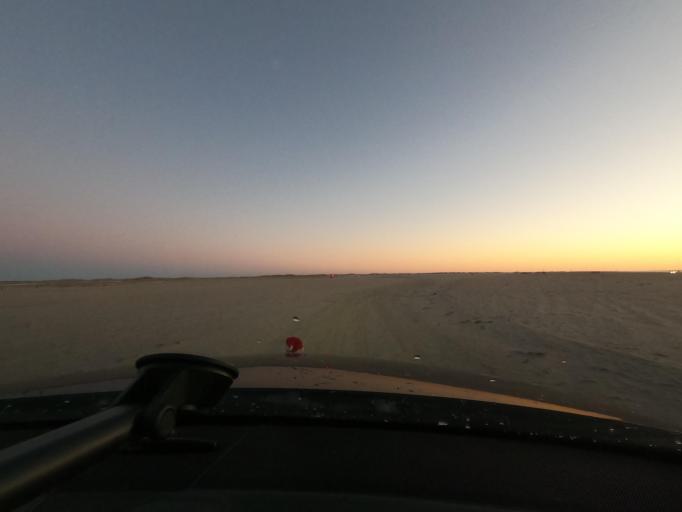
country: DE
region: Schleswig-Holstein
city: List
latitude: 55.1555
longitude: 8.4783
